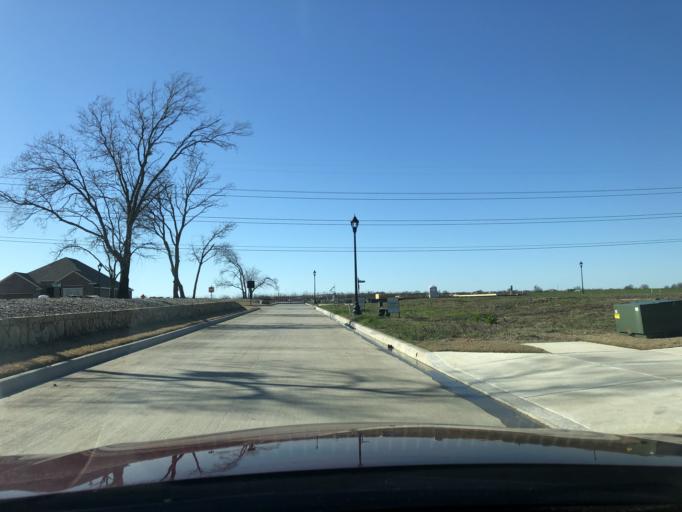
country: US
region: Texas
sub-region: Tarrant County
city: Haslet
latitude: 32.9490
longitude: -97.3999
